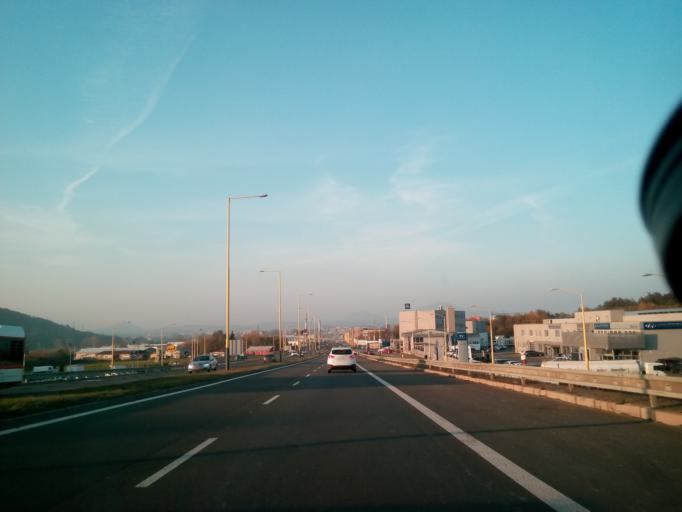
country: SK
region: Presovsky
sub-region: Okres Presov
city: Presov
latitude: 48.9577
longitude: 21.2571
